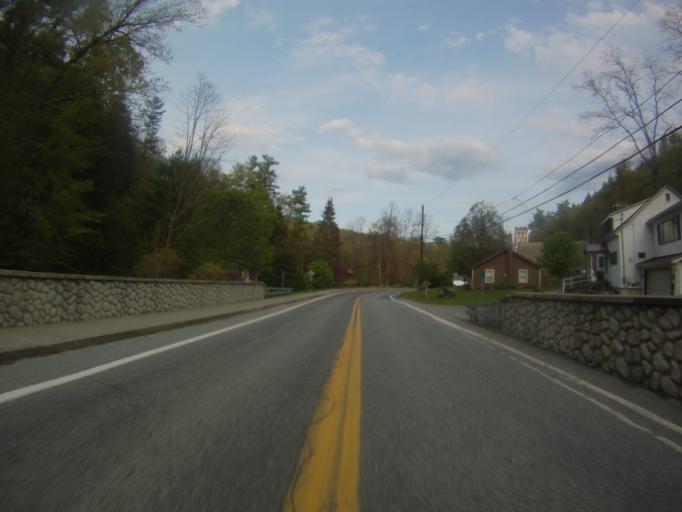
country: US
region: New York
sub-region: Essex County
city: Ticonderoga
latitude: 43.7491
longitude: -73.5042
